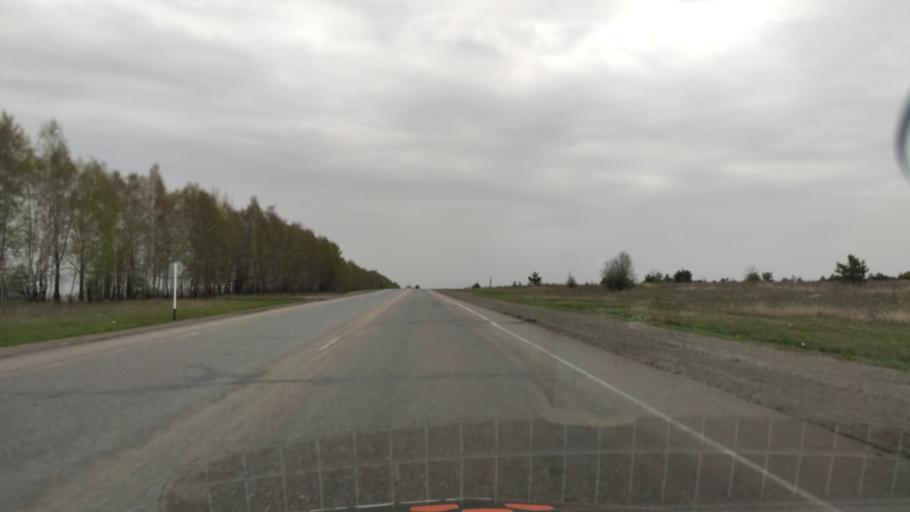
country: RU
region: Kursk
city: Gorshechnoye
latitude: 51.4532
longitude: 37.9178
